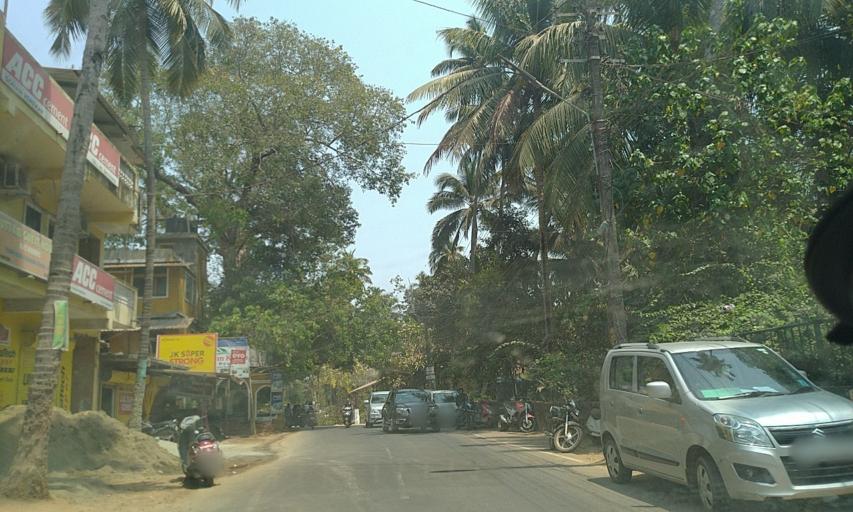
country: IN
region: Goa
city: Calangute
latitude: 15.5476
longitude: 73.7662
